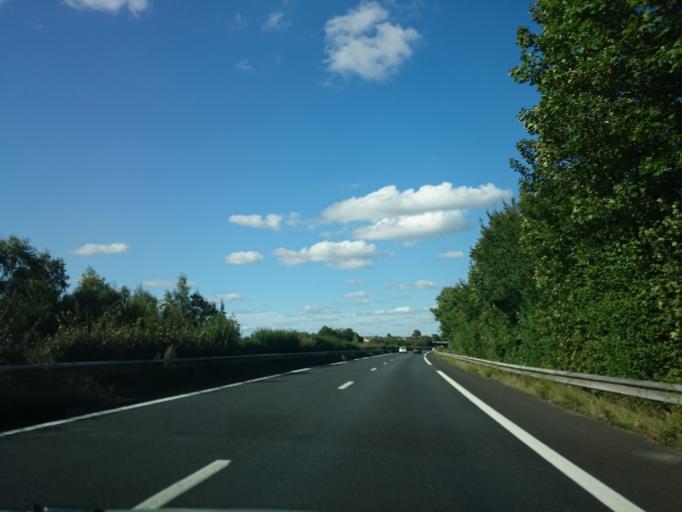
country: FR
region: Pays de la Loire
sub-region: Departement de la Loire-Atlantique
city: Nozay
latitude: 47.5648
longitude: -1.6347
